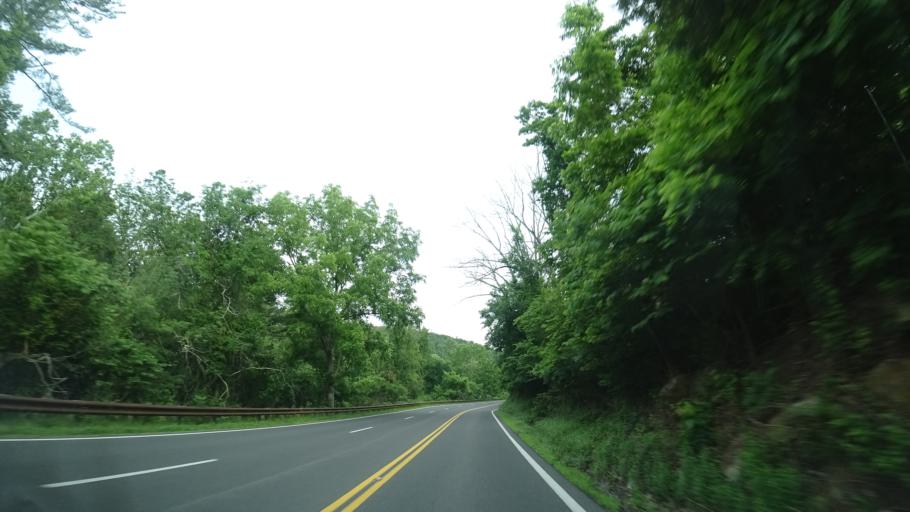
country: US
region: Virginia
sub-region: Page County
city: Luray
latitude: 38.6586
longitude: -78.3696
